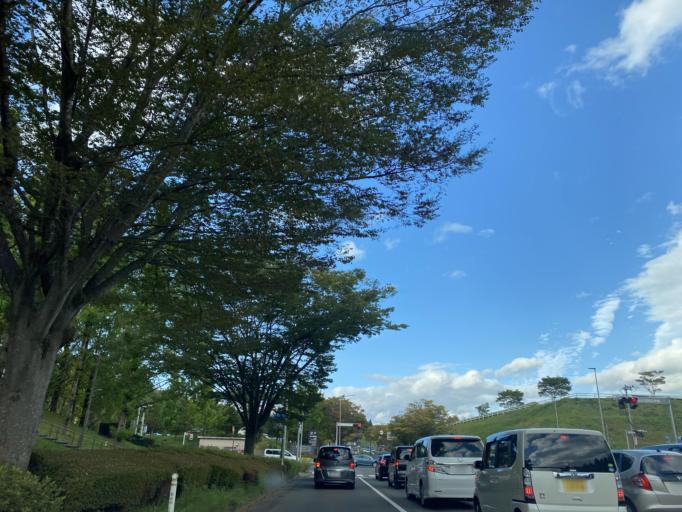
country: JP
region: Miyagi
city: Tomiya
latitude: 38.3428
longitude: 140.8391
